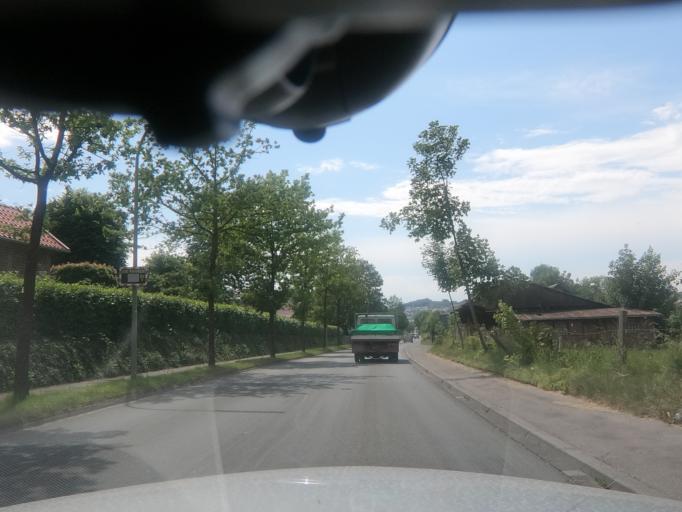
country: DE
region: North Rhine-Westphalia
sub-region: Regierungsbezirk Arnsberg
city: Sundern
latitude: 51.3196
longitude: 8.0272
